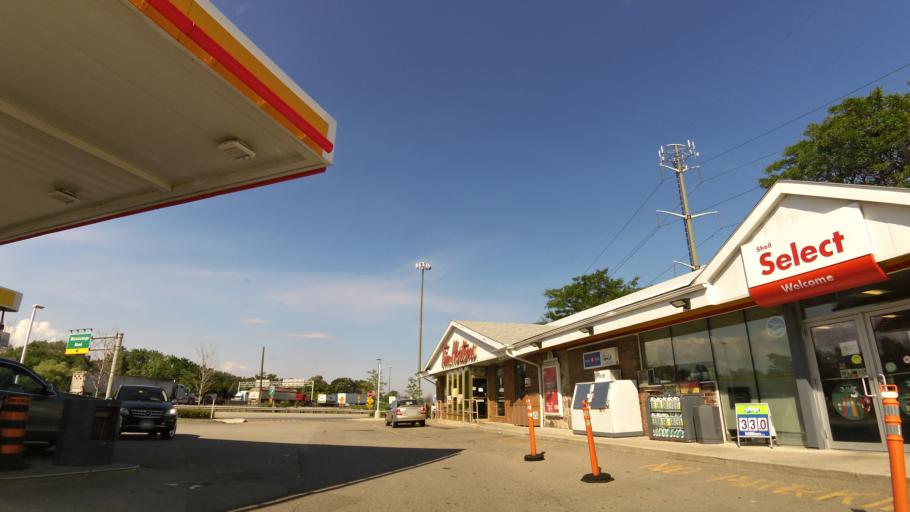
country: CA
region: Ontario
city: Mississauga
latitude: 43.5499
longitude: -79.6162
